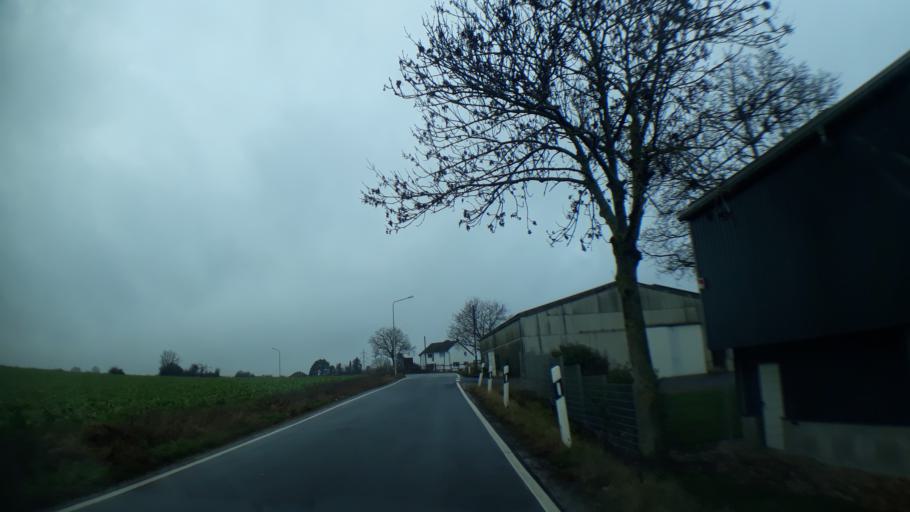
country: DE
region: North Rhine-Westphalia
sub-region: Regierungsbezirk Koln
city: Kreuzau
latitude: 50.7569
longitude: 6.4758
